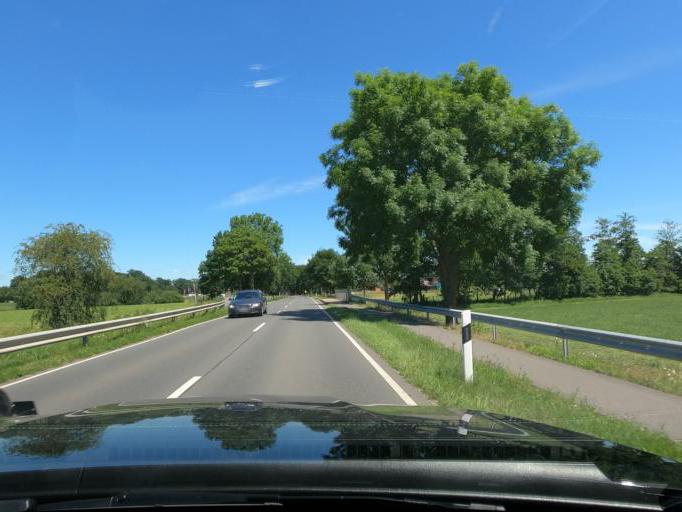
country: DE
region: Lower Saxony
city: Eicklingen
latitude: 52.5454
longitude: 10.1707
